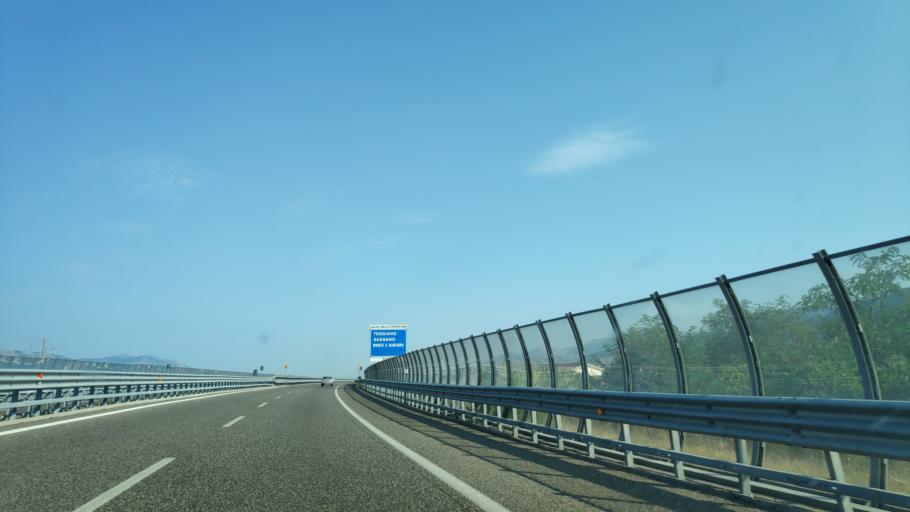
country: IT
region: Campania
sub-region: Provincia di Salerno
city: Sala Consilina
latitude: 40.4117
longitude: 15.5633
